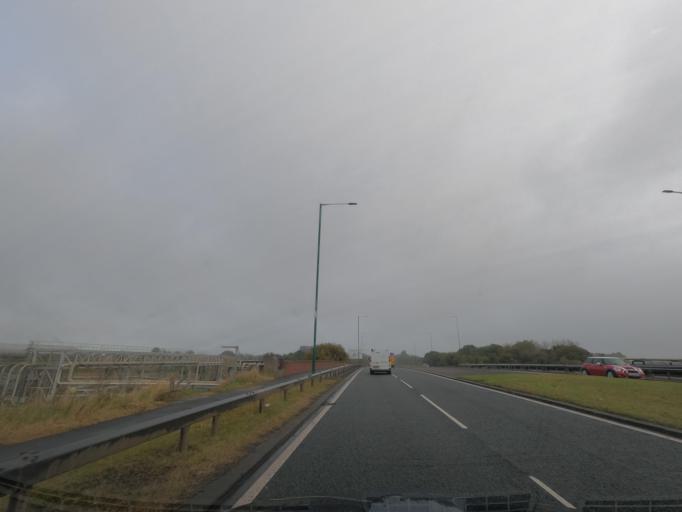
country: GB
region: England
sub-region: Redcar and Cleveland
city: South Bank
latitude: 54.6041
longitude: -1.1139
